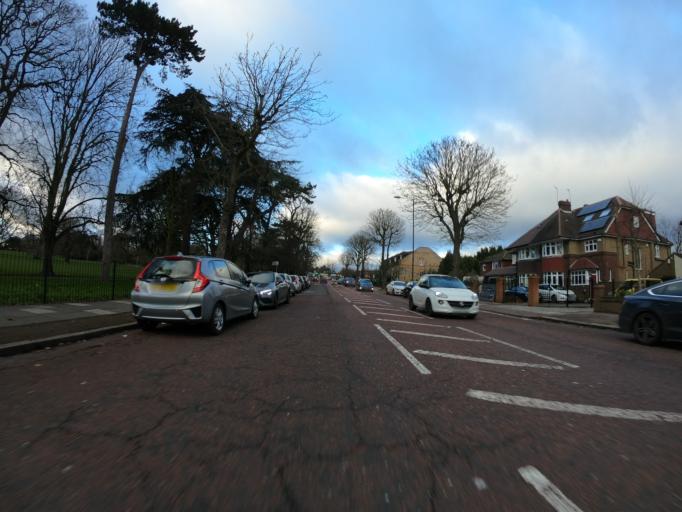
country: GB
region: England
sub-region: Greater London
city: Welling
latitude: 51.4490
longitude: 0.0810
